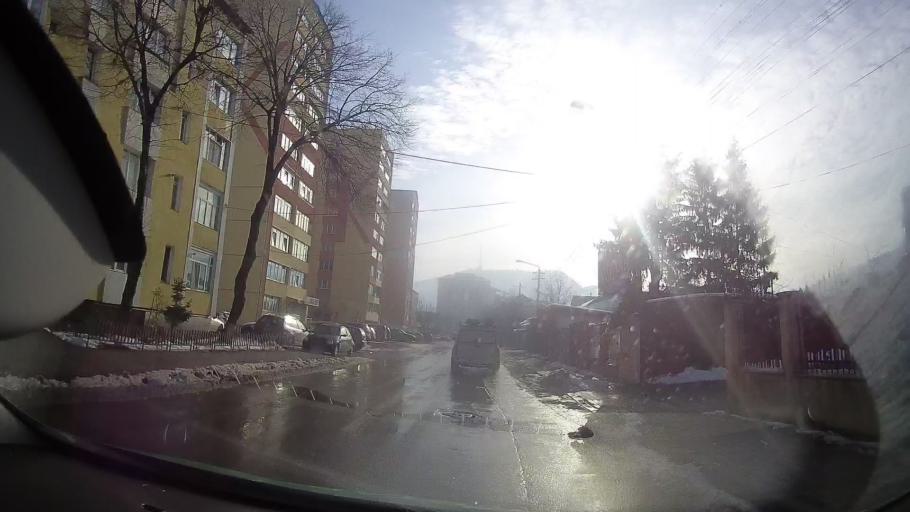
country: RO
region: Neamt
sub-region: Municipiul Piatra-Neamt
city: Valeni
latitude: 46.9423
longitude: 26.3822
